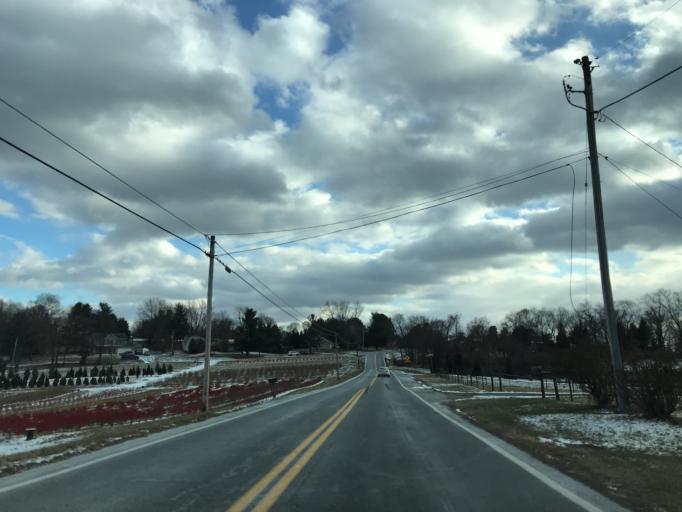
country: US
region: Maryland
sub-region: Harford County
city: Bel Air North
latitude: 39.6445
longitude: -76.3818
